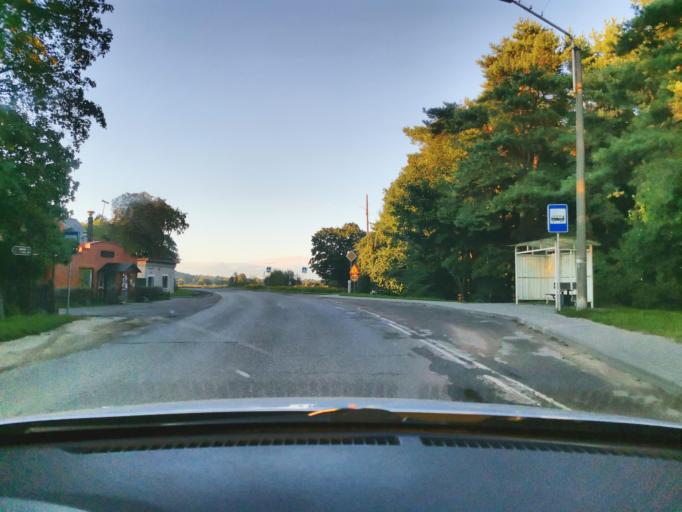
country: RU
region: Kaliningrad
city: Chernyakhovsk
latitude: 54.6500
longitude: 21.8137
